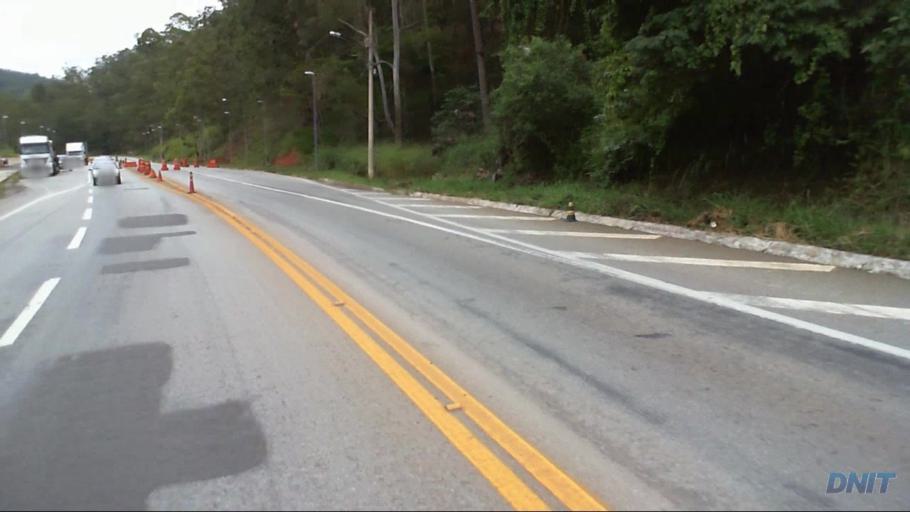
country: BR
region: Minas Gerais
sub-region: Joao Monlevade
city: Joao Monlevade
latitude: -19.8502
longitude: -43.1523
